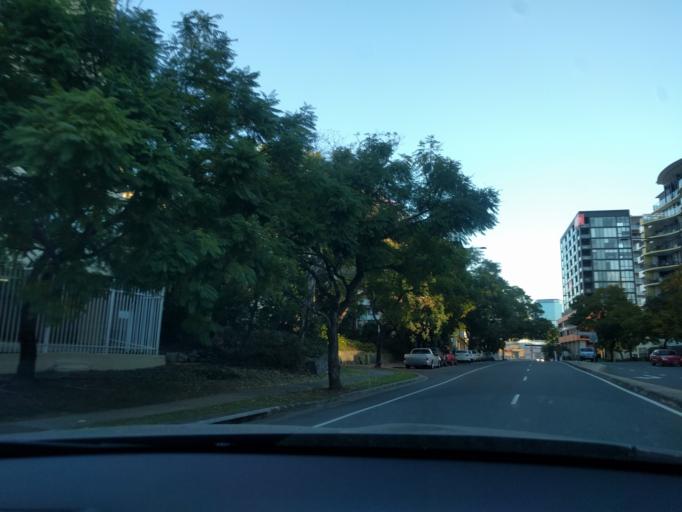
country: AU
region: Queensland
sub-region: Brisbane
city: Toowong
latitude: -27.4801
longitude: 152.9965
